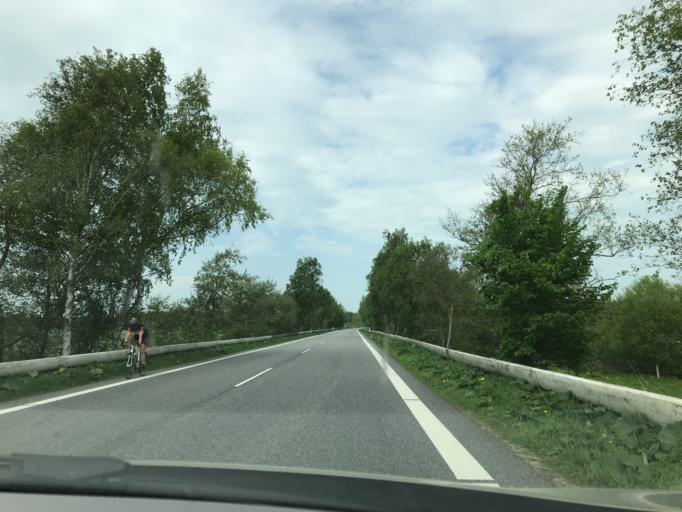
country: DK
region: South Denmark
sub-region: Assens Kommune
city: Assens
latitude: 55.3195
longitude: 9.9382
